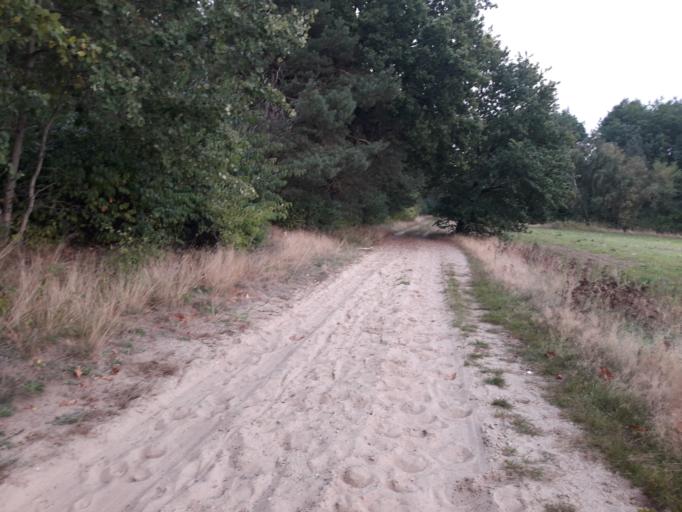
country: DE
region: Schleswig-Holstein
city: Wiershop
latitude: 53.4297
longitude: 10.4321
